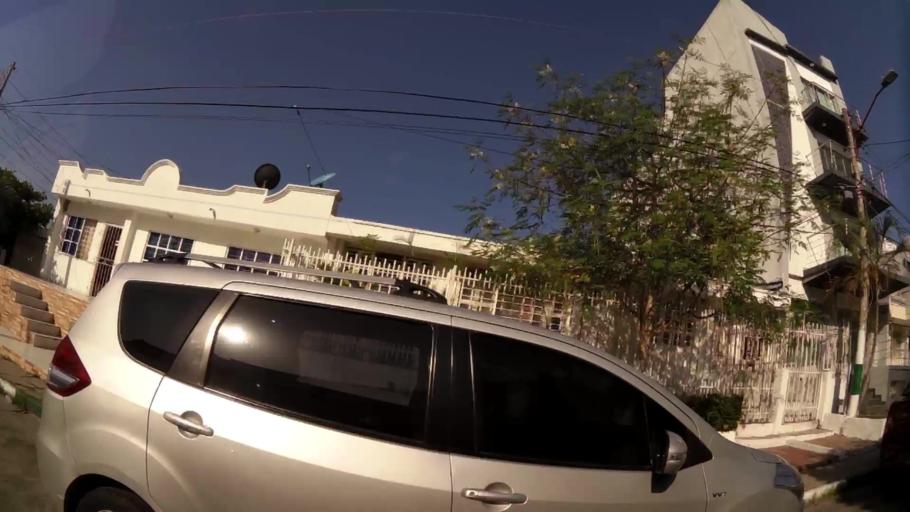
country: CO
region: Bolivar
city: Cartagena
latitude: 10.3920
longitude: -75.5189
